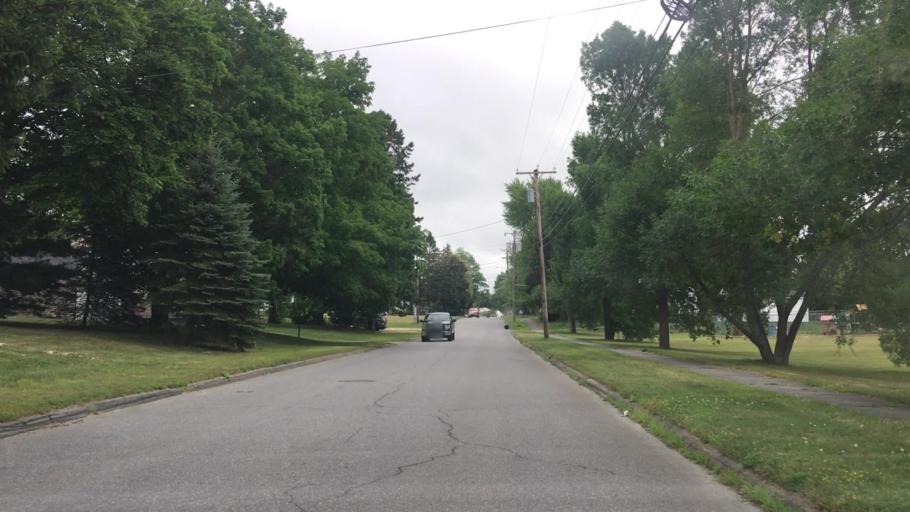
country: US
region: Maine
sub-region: Penobscot County
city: Brewer
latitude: 44.7876
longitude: -68.7516
